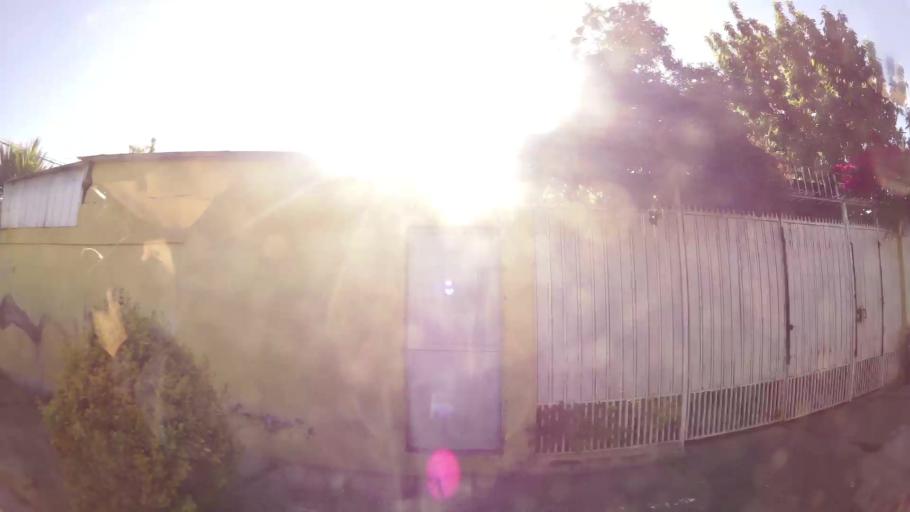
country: CL
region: Santiago Metropolitan
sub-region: Provincia de Maipo
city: San Bernardo
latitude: -33.5465
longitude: -70.6806
